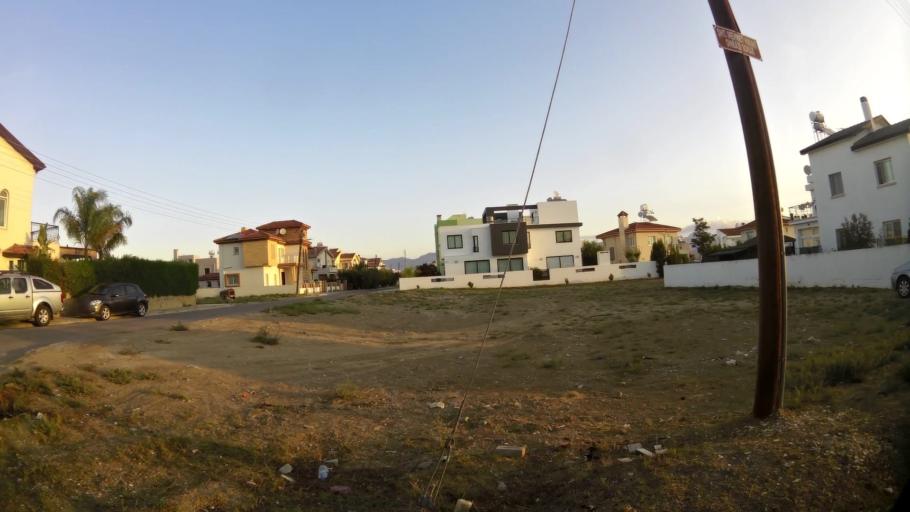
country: CY
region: Lefkosia
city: Nicosia
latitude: 35.1905
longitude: 33.3219
